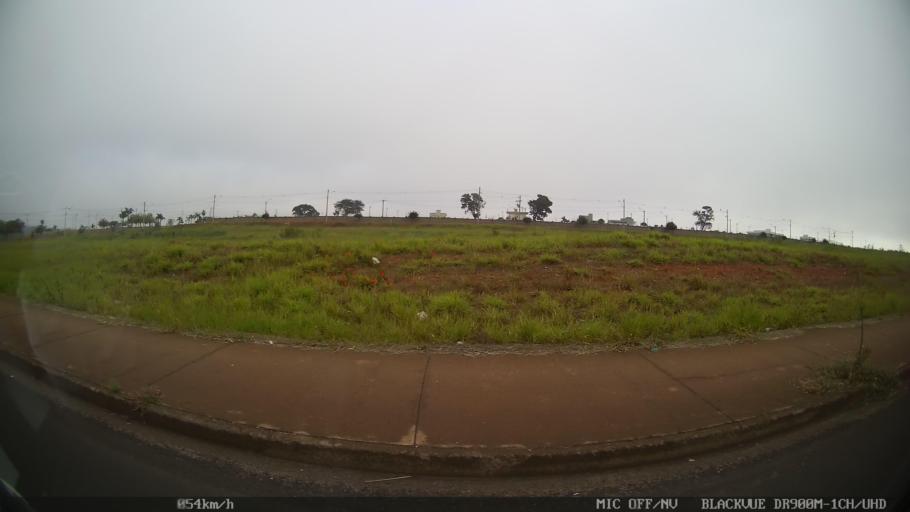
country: BR
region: Sao Paulo
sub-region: Sao Jose Do Rio Preto
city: Sao Jose do Rio Preto
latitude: -20.8545
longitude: -49.3710
